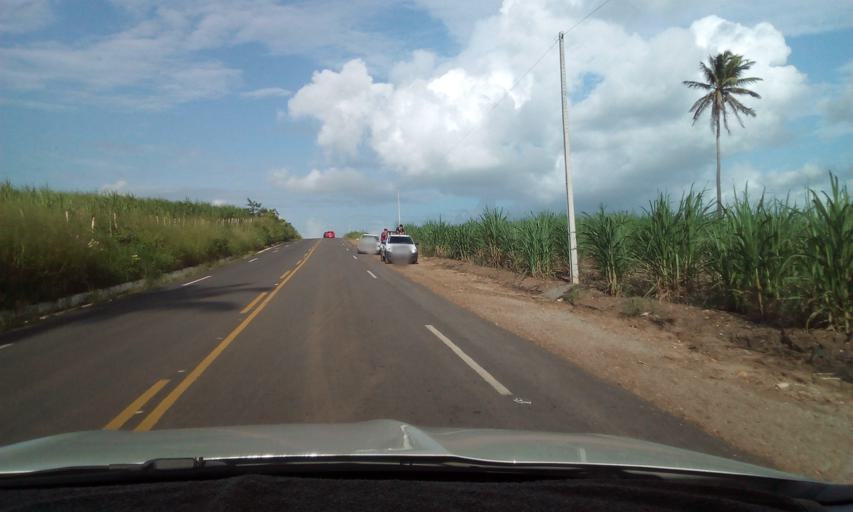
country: BR
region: Paraiba
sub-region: Mamanguape
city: Mamanguape
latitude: -6.8157
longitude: -35.2186
